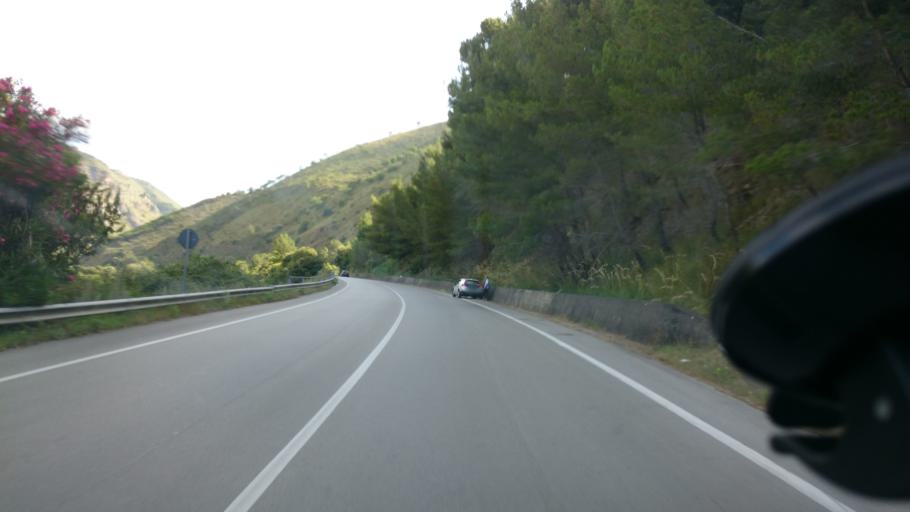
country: IT
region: Campania
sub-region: Provincia di Salerno
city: Centola
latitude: 40.0456
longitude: 15.3259
